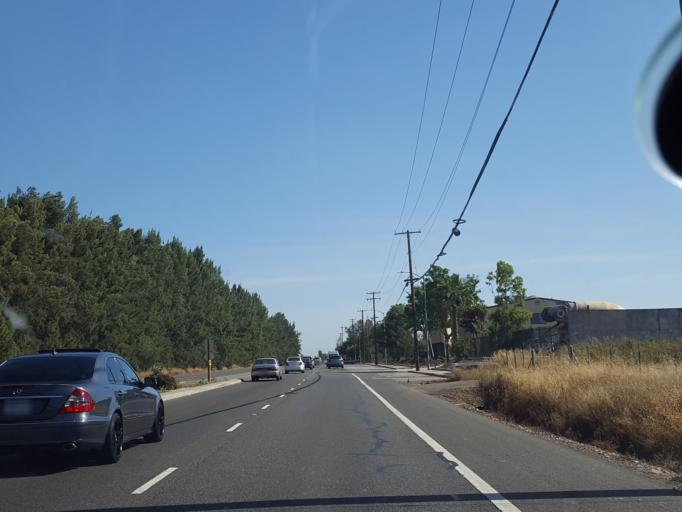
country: US
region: California
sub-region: Sacramento County
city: Vineyard
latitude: 38.5064
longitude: -121.3351
